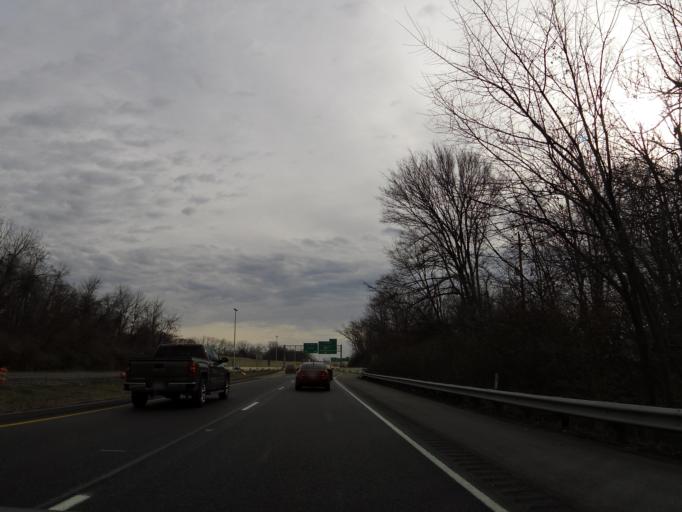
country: US
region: Indiana
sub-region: Marion County
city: Speedway
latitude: 39.8115
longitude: -86.2868
